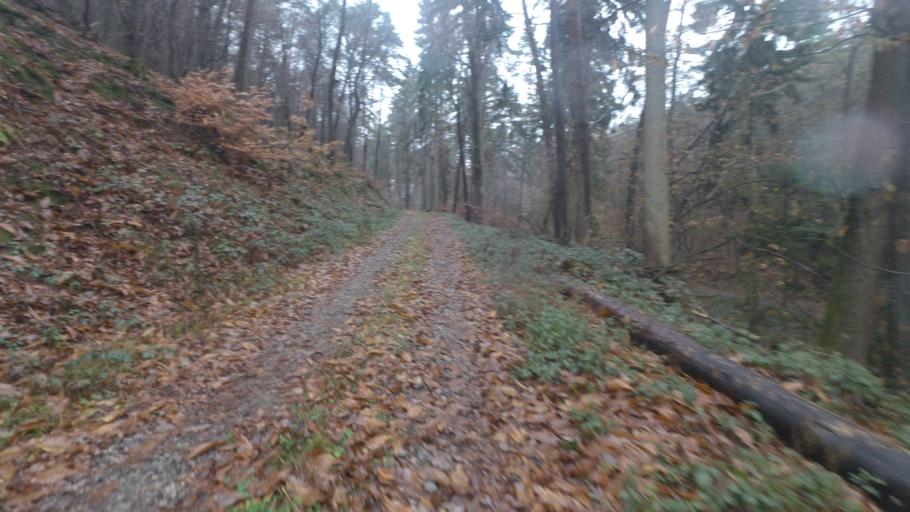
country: DE
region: Rheinland-Pfalz
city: Deidesheim
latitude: 49.4040
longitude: 8.1572
